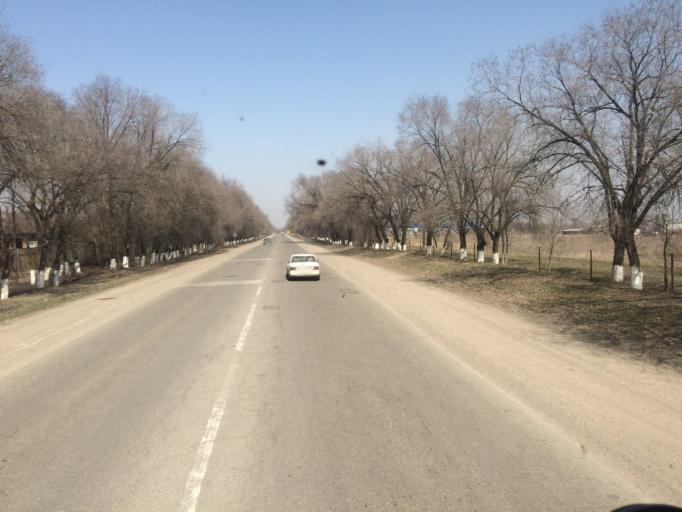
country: KZ
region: Almaty Oblysy
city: Burunday
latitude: 43.2309
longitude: 76.6629
